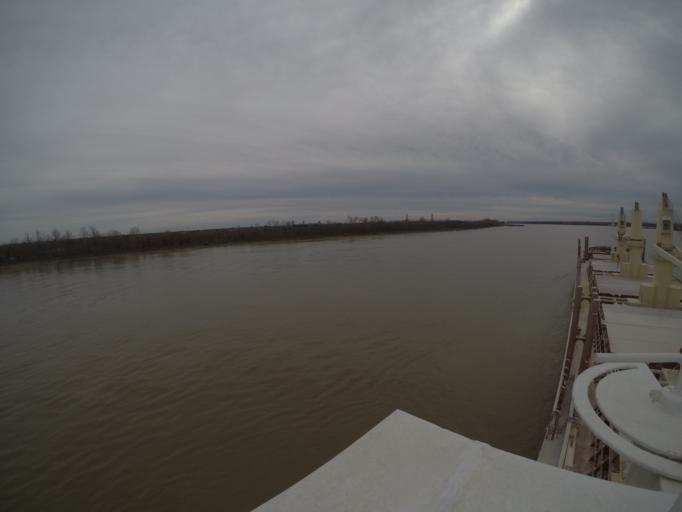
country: US
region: Louisiana
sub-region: Saint Charles Parish
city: New Sarpy
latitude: 29.9690
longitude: -90.3956
